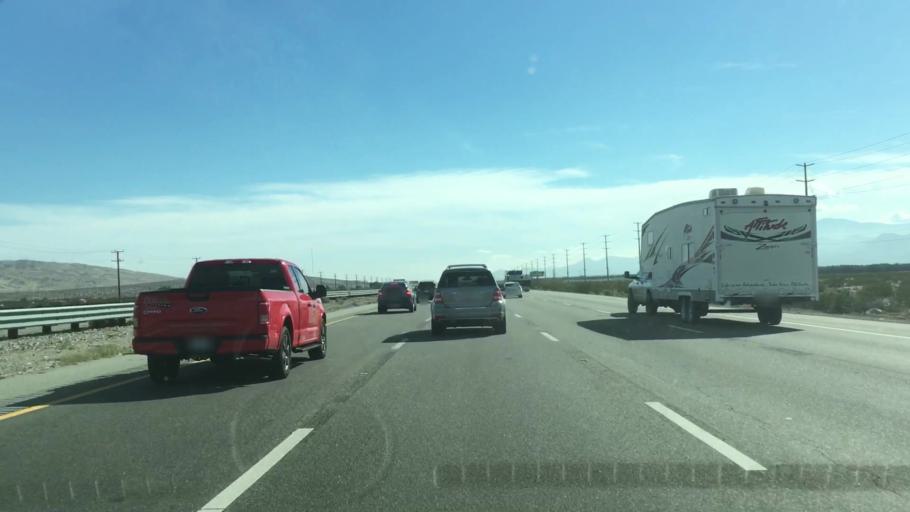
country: US
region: California
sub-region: Riverside County
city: Garnet
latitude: 33.8922
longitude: -116.5187
